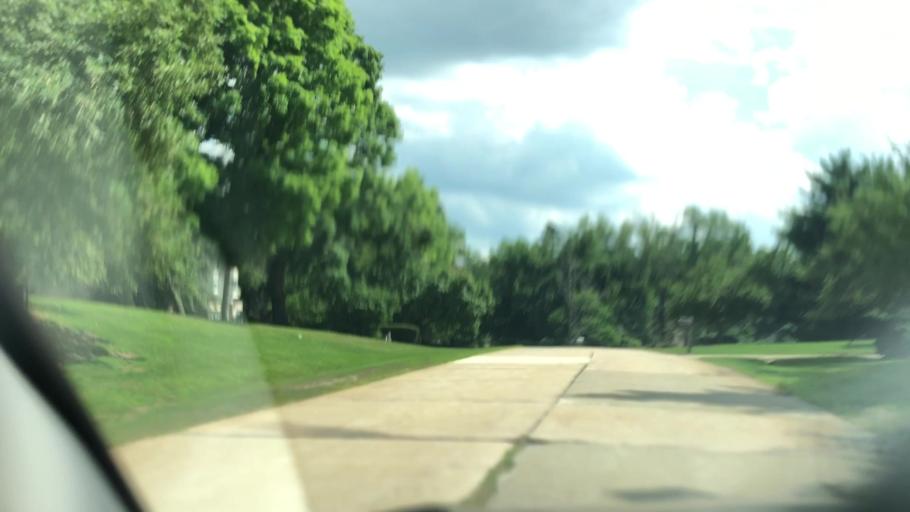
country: US
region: Ohio
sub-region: Summit County
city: Montrose-Ghent
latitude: 41.1620
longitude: -81.6401
